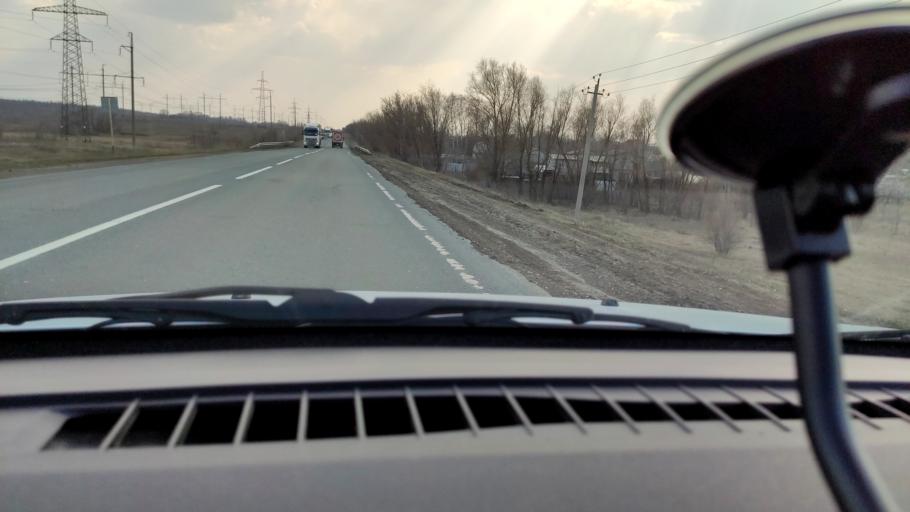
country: RU
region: Samara
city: Smyshlyayevka
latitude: 53.0901
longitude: 50.3962
